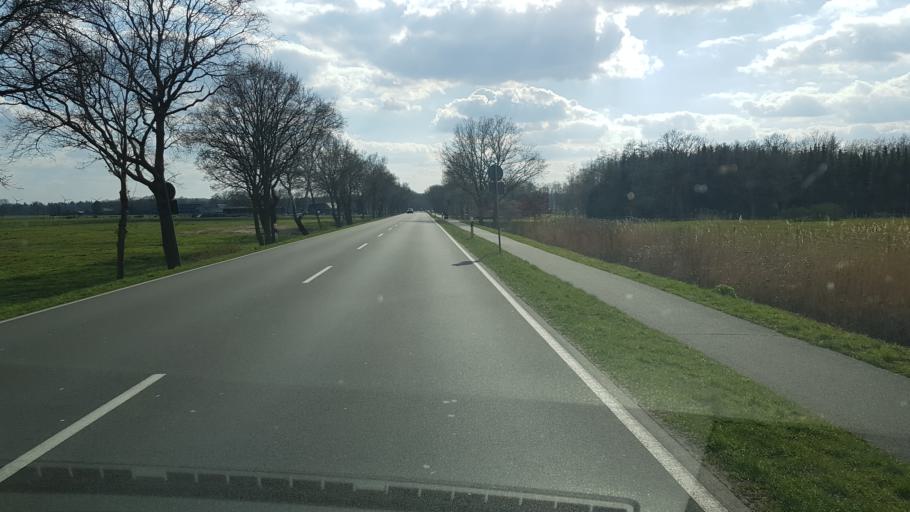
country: DE
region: Lower Saxony
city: Rastede
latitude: 53.2422
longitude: 8.2884
